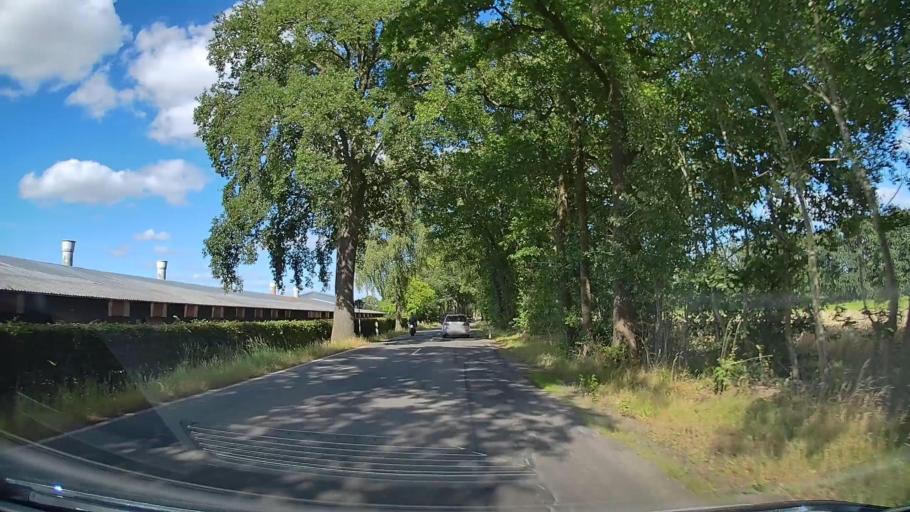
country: DE
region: Lower Saxony
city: Menslage
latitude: 52.6286
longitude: 7.7823
